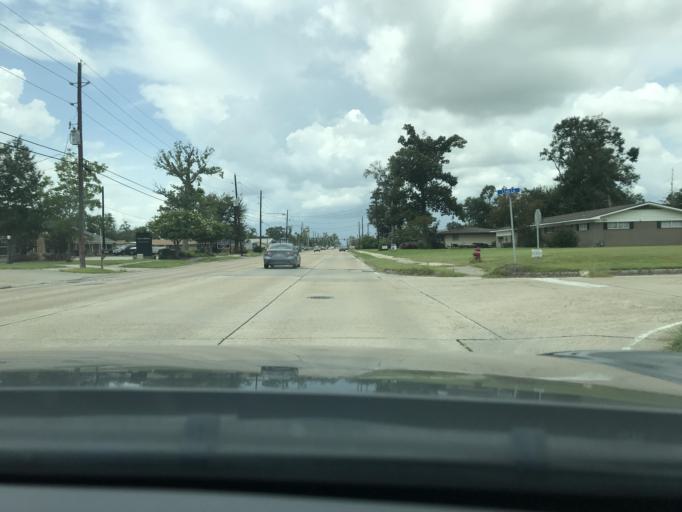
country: US
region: Louisiana
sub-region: Calcasieu Parish
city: Sulphur
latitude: 30.2277
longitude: -93.3305
